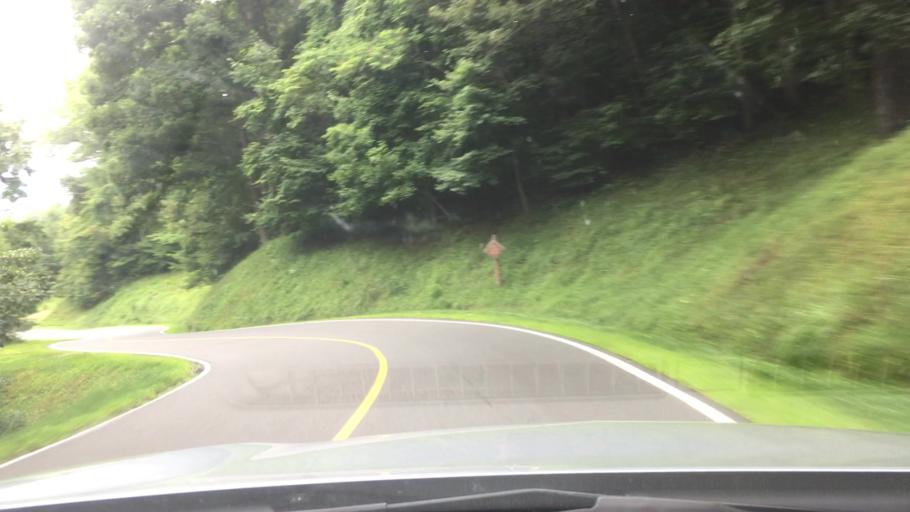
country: US
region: North Carolina
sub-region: Yancey County
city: Burnsville
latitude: 35.8918
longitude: -82.3523
